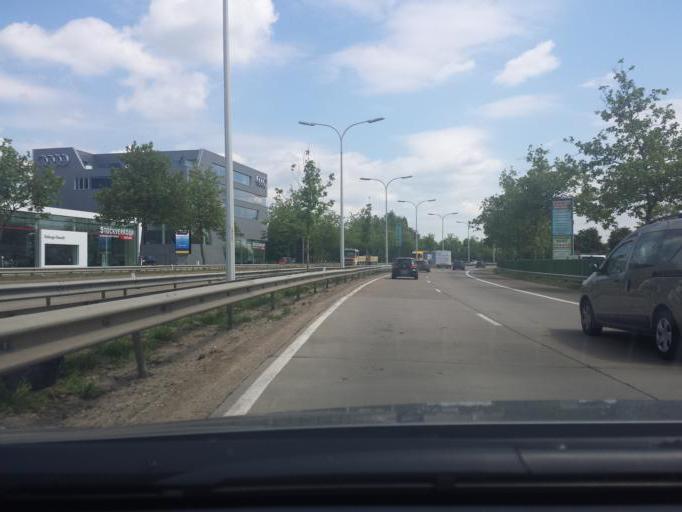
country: BE
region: Flanders
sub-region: Provincie Limburg
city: Hasselt
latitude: 50.9412
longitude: 5.3214
